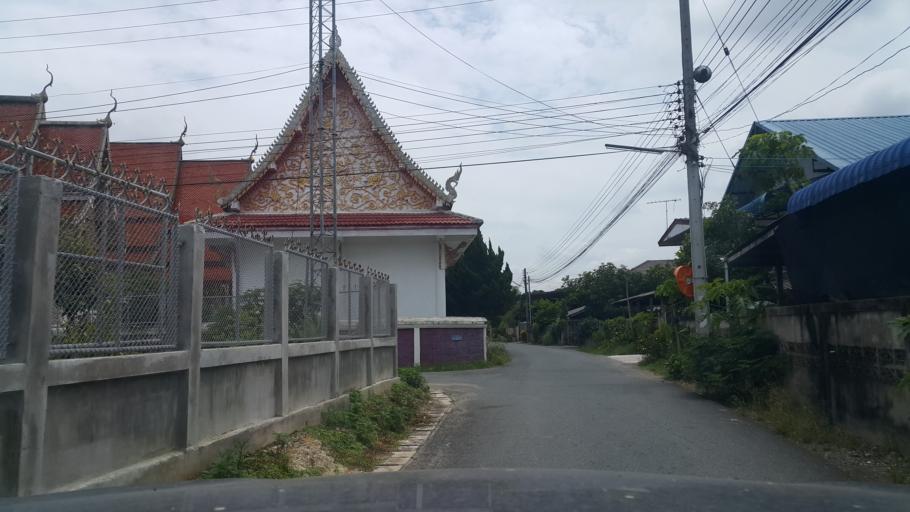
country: TH
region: Chiang Mai
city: San Kamphaeng
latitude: 18.6959
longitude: 99.1623
